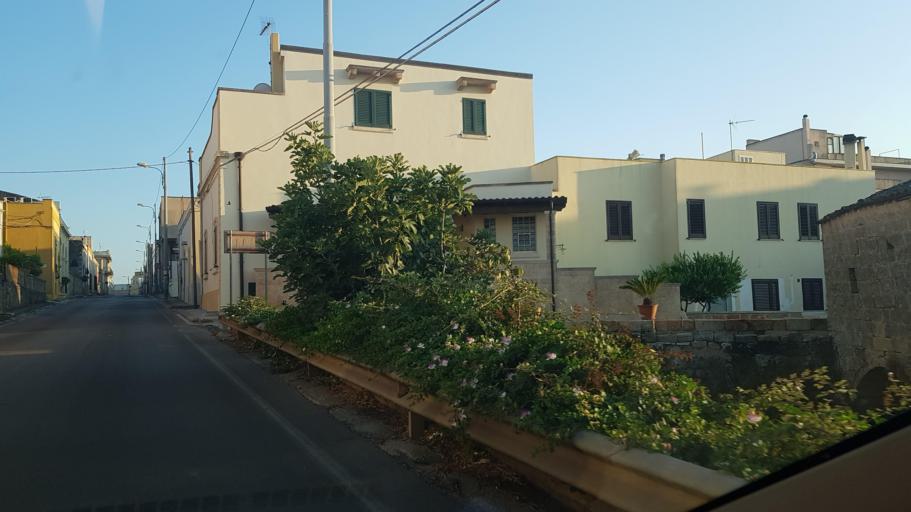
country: IT
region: Apulia
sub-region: Provincia di Lecce
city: Lucugnano
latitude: 39.9372
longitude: 18.3194
